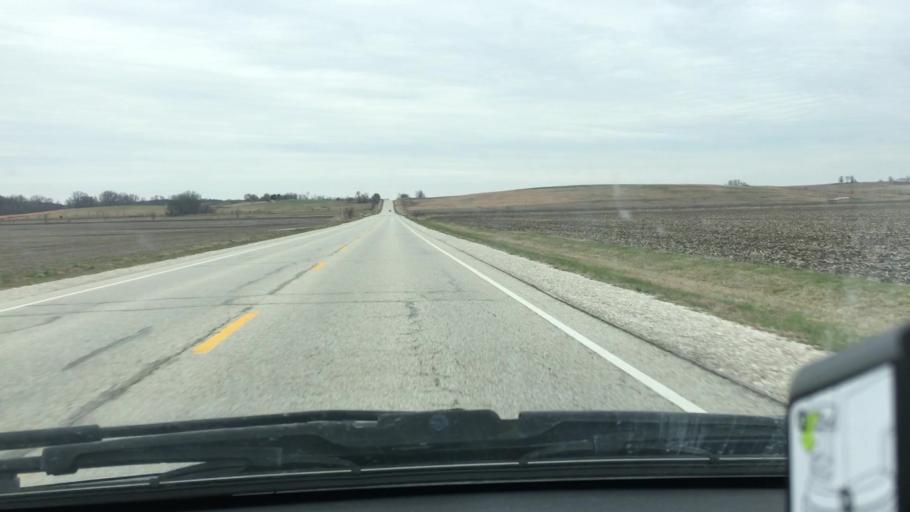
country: US
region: Indiana
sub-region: Greene County
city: Bloomfield
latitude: 39.0033
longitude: -87.0163
